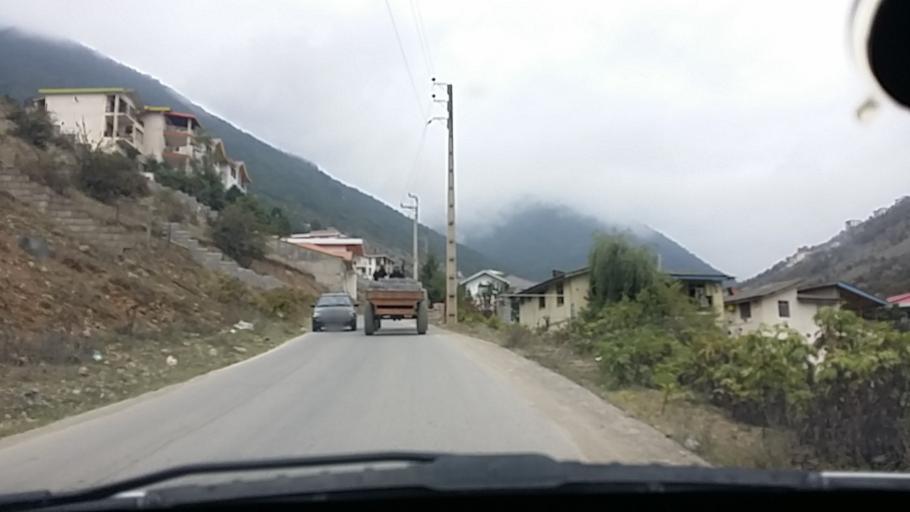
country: IR
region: Mazandaran
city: `Abbasabad
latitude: 36.4775
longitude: 51.1397
